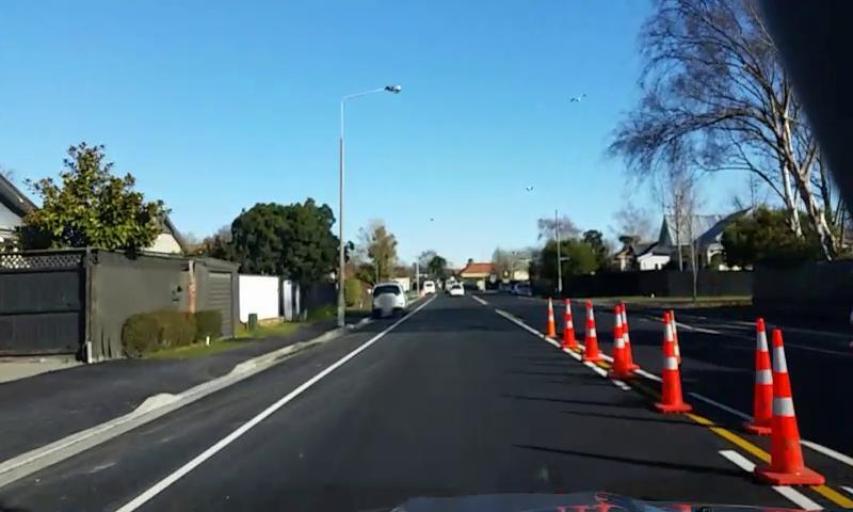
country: NZ
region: Canterbury
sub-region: Christchurch City
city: Christchurch
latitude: -43.5081
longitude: 172.6451
